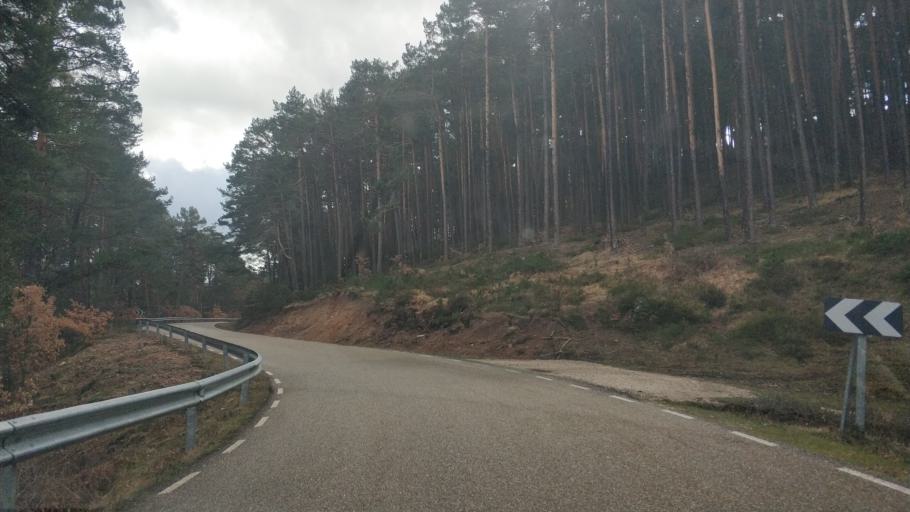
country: ES
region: Castille and Leon
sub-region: Provincia de Burgos
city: Quintanar de la Sierra
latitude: 42.0100
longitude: -3.0203
